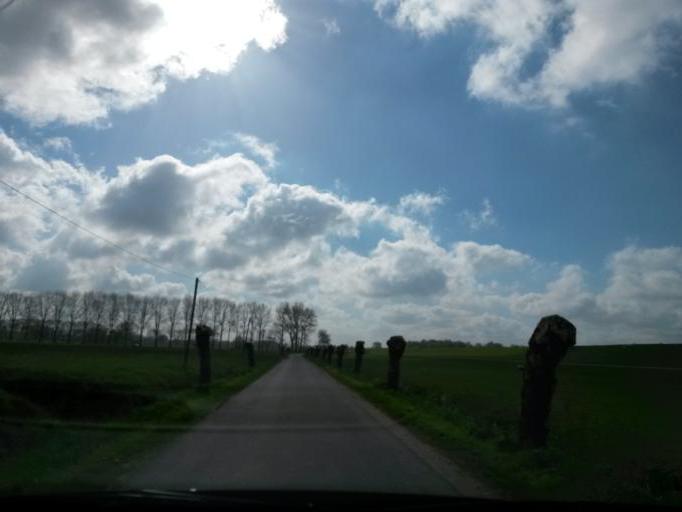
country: DE
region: Schleswig-Holstein
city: Hetlingen
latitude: 53.5833
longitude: 9.6602
